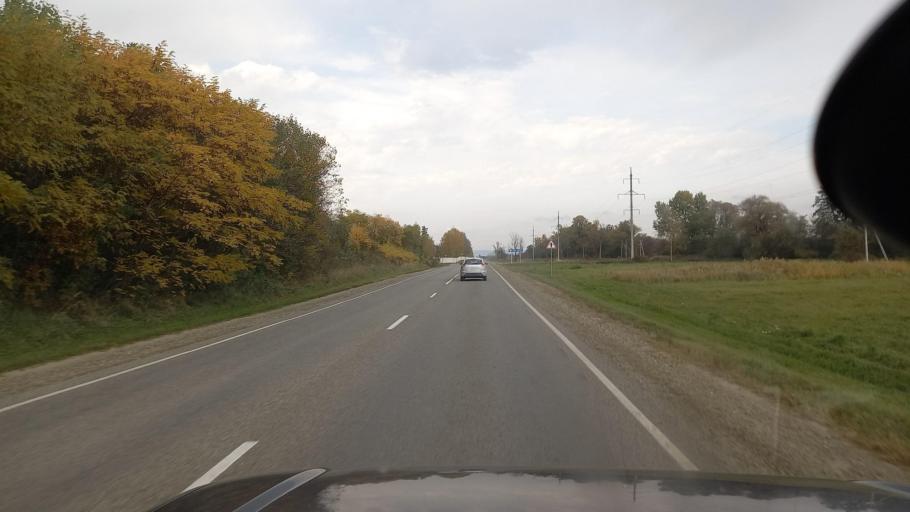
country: RU
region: Krasnodarskiy
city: Shedok
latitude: 44.1820
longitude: 40.8417
